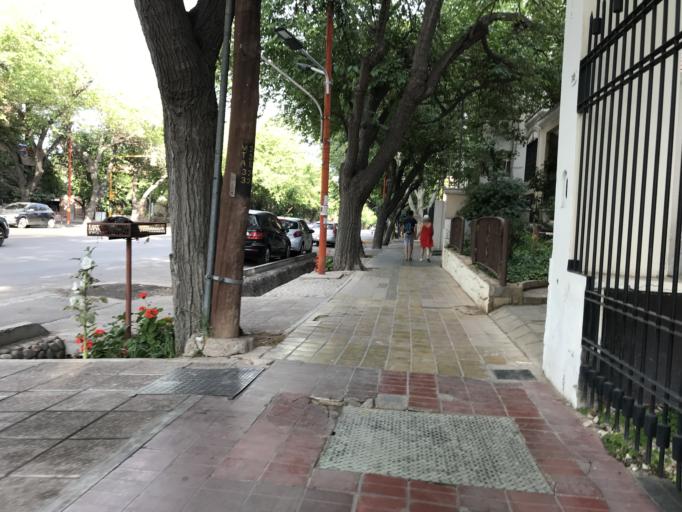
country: AR
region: Mendoza
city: Mendoza
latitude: -32.8880
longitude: -68.8544
